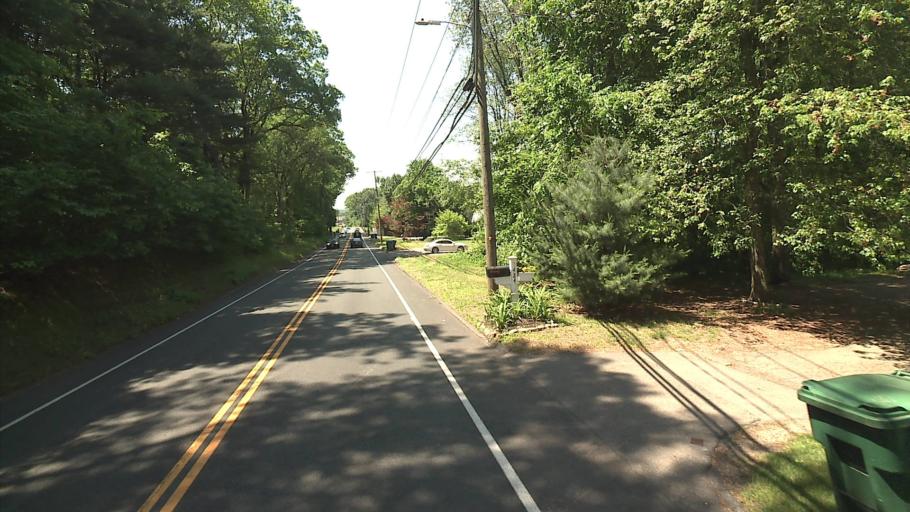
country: US
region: Connecticut
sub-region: Hartford County
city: Manchester
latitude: 41.8188
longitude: -72.5374
